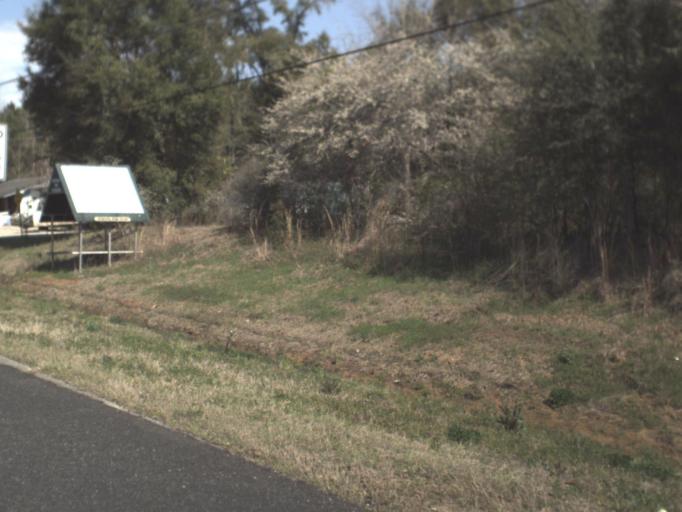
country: US
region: Florida
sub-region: Gadsden County
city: Havana
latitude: 30.6000
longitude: -84.4178
